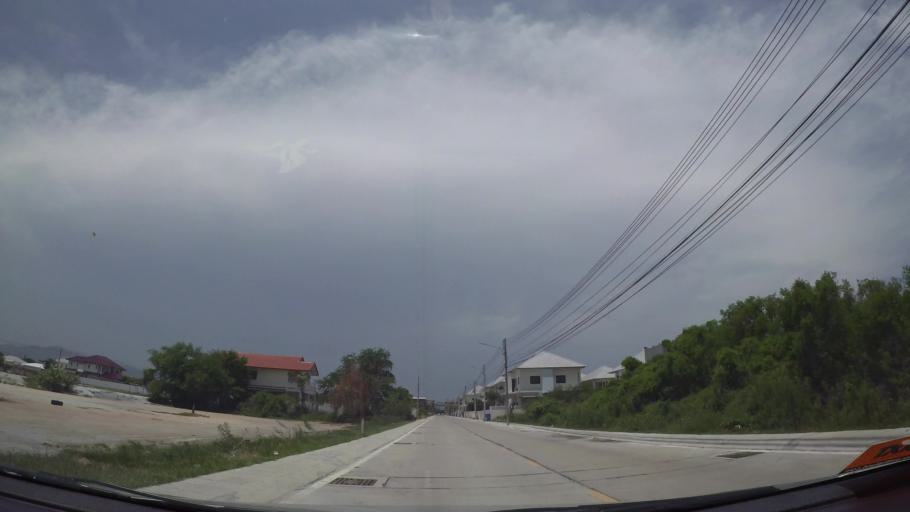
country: TH
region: Chon Buri
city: Chon Buri
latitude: 13.3408
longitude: 100.9466
